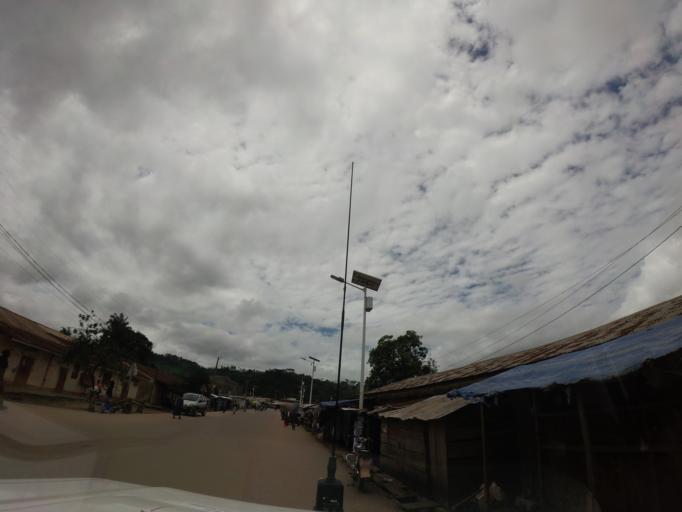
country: GN
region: Nzerekore
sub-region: Macenta
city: Macenta
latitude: 8.5467
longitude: -9.4695
